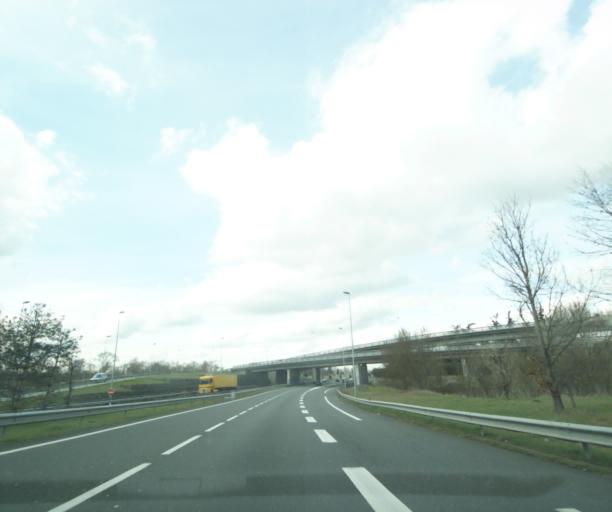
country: FR
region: Midi-Pyrenees
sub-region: Departement de la Haute-Garonne
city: Ramonville-Saint-Agne
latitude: 43.5536
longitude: 1.4934
